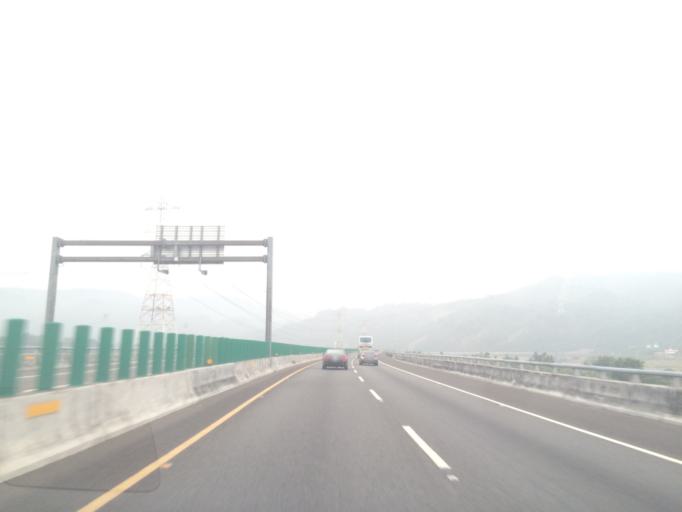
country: TW
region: Taiwan
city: Zhongxing New Village
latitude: 23.9925
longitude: 120.7522
